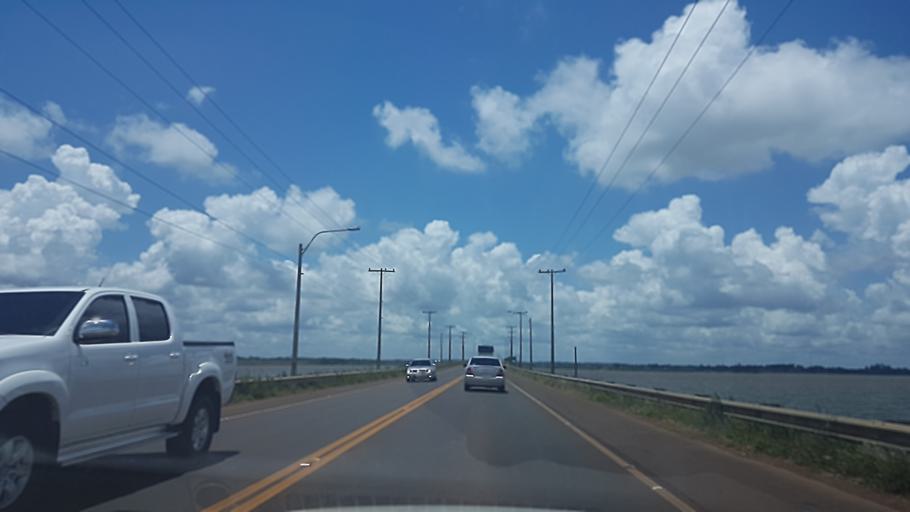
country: PY
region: Itapua
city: Carmen del Parana
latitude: -27.2032
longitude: -56.1733
